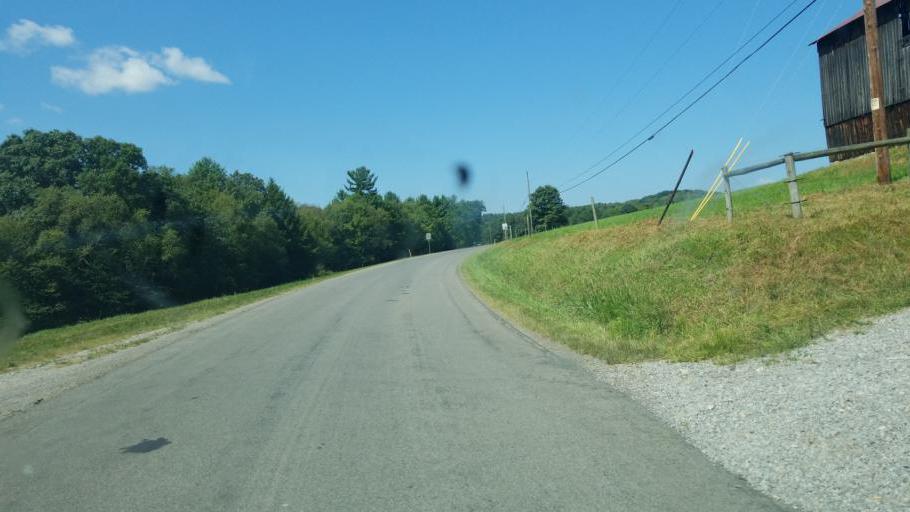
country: US
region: Pennsylvania
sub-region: Clarion County
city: Clarion
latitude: 41.1729
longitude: -79.4164
